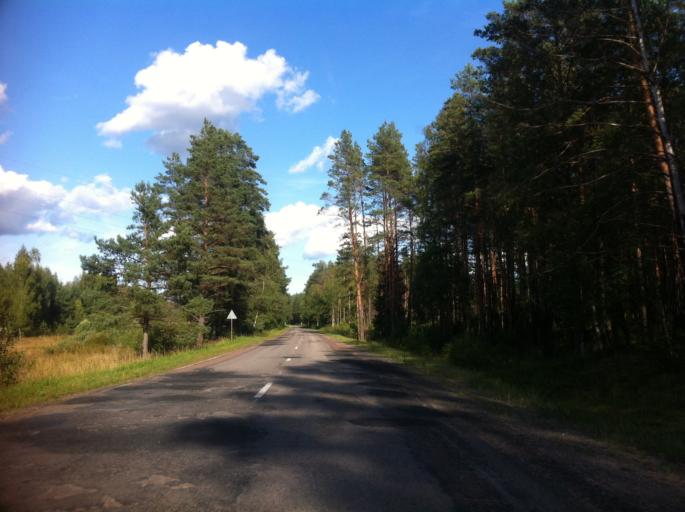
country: RU
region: Pskov
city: Izborsk
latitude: 57.8030
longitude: 27.7897
